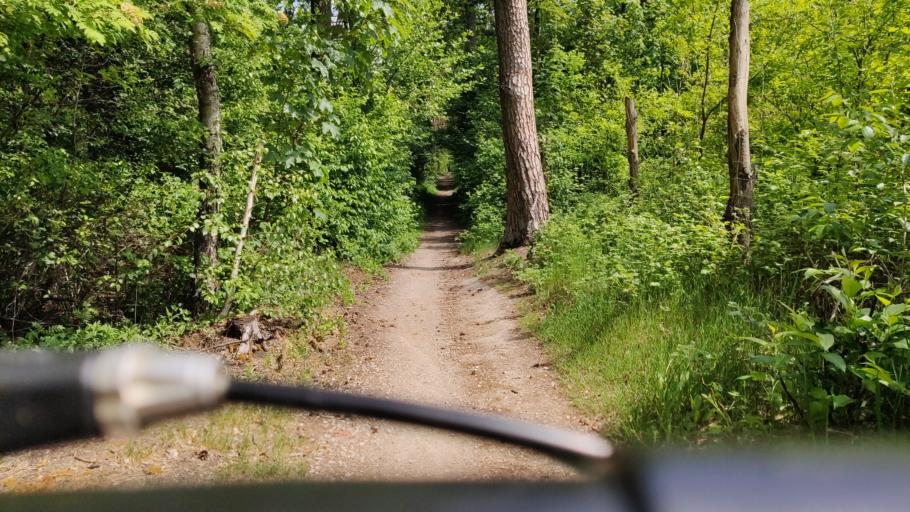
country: PL
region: Kujawsko-Pomorskie
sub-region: Wloclawek
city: Wloclawek
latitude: 52.6366
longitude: 19.1140
